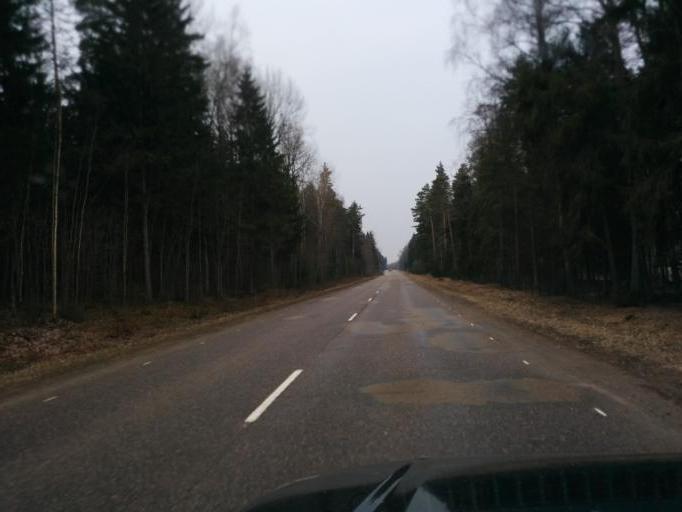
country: LV
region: Ikskile
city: Ikskile
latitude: 56.8073
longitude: 24.4921
